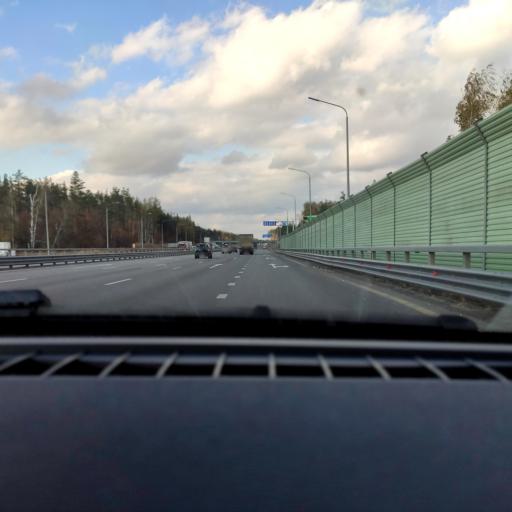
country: RU
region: Voronezj
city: Somovo
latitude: 51.6866
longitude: 39.3030
